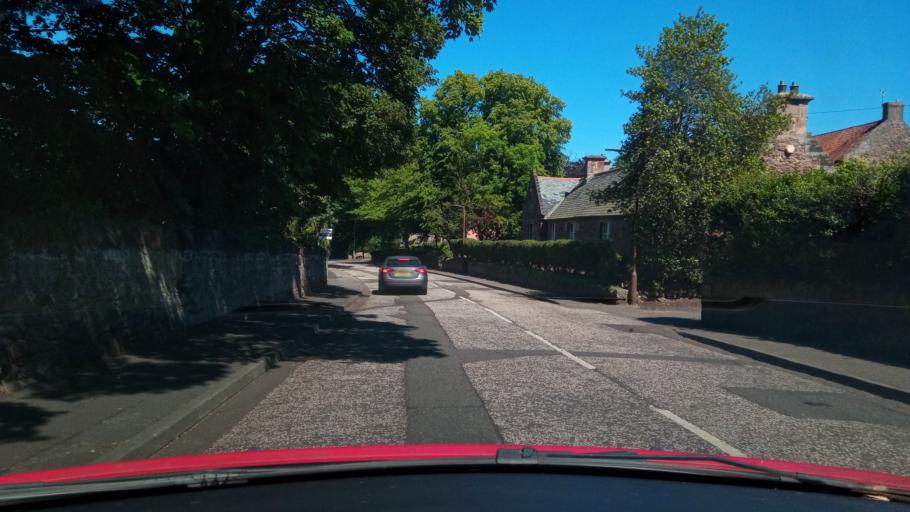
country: GB
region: Scotland
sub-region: East Lothian
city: Gullane
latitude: 56.0447
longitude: -2.7830
